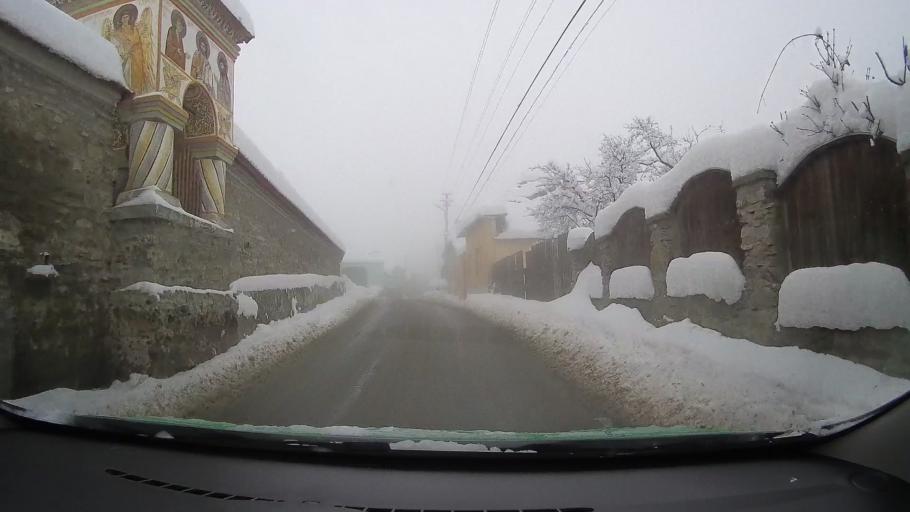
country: RO
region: Sibiu
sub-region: Comuna Poiana Sibiului
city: Poiana Sibiului
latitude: 45.8015
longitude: 23.7799
